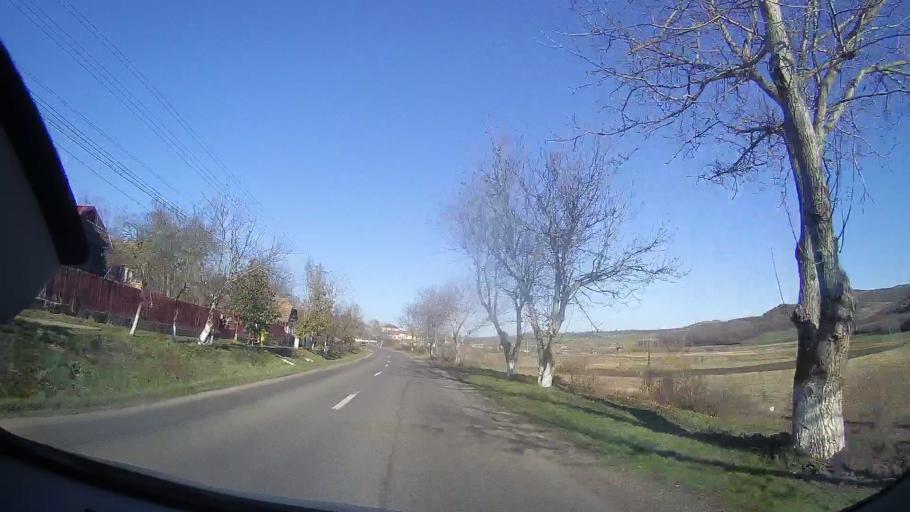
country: RO
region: Mures
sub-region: Comuna Sarmasu
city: Balda
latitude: 46.7266
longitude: 24.1440
